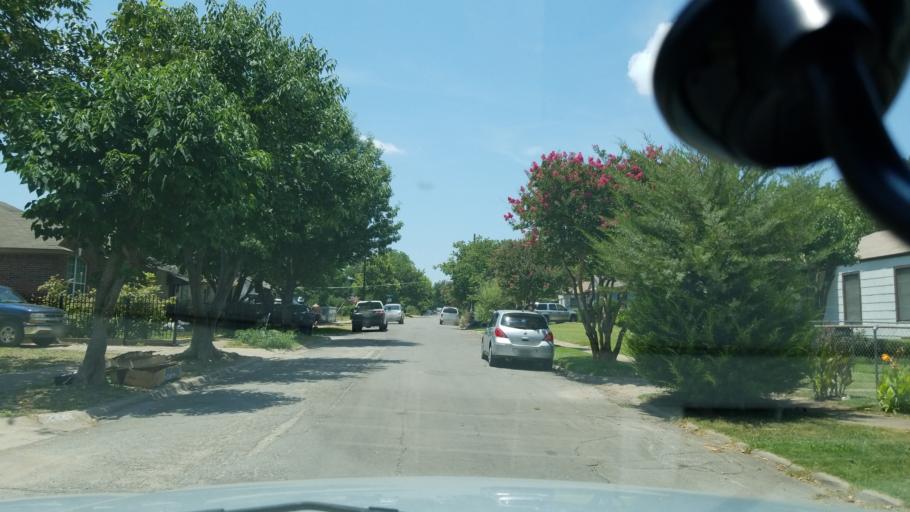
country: US
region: Texas
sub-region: Dallas County
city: Cockrell Hill
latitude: 32.7272
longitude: -96.8650
